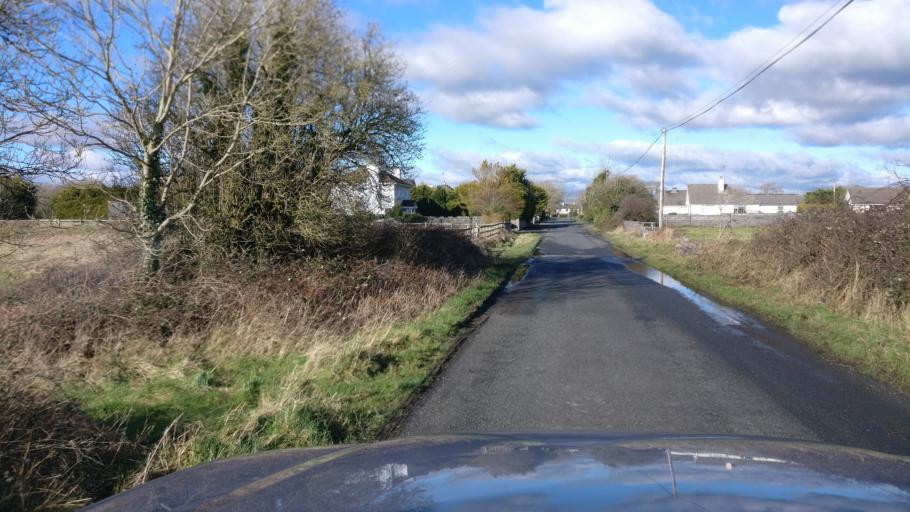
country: IE
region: Connaught
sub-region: County Galway
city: Oranmore
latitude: 53.2762
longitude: -8.9060
